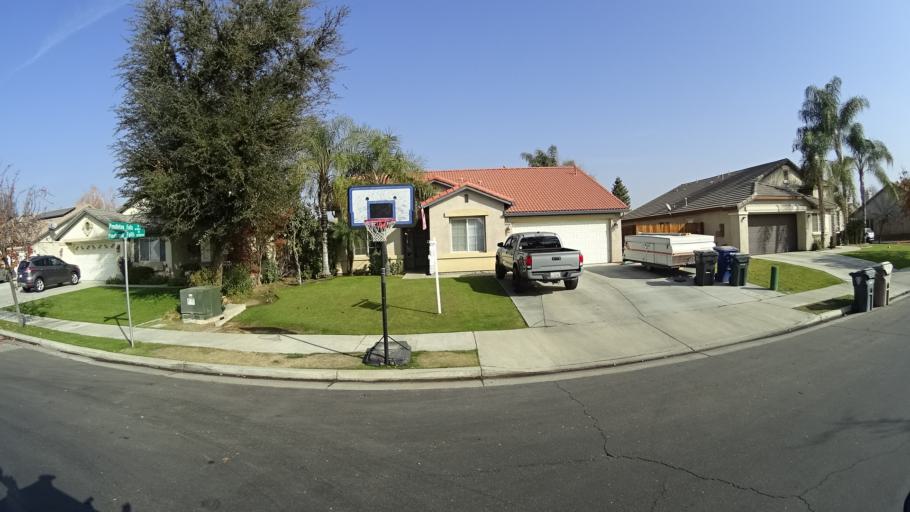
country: US
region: California
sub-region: Kern County
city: Greenacres
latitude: 35.4148
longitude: -119.1208
